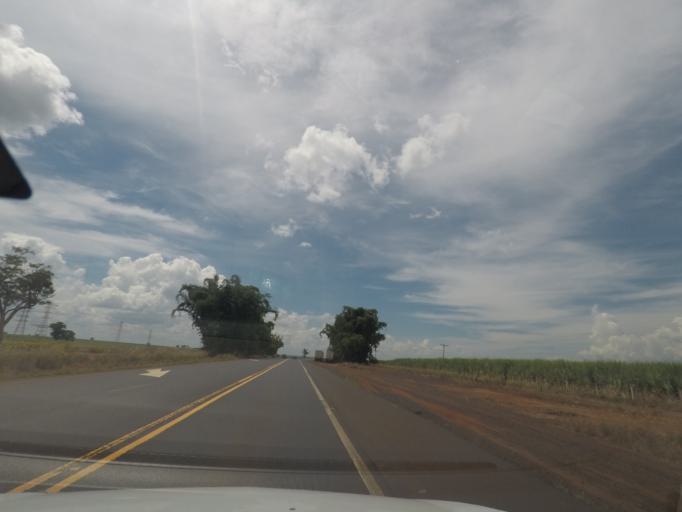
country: BR
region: Sao Paulo
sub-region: Barretos
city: Barretos
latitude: -20.2764
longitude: -48.6720
